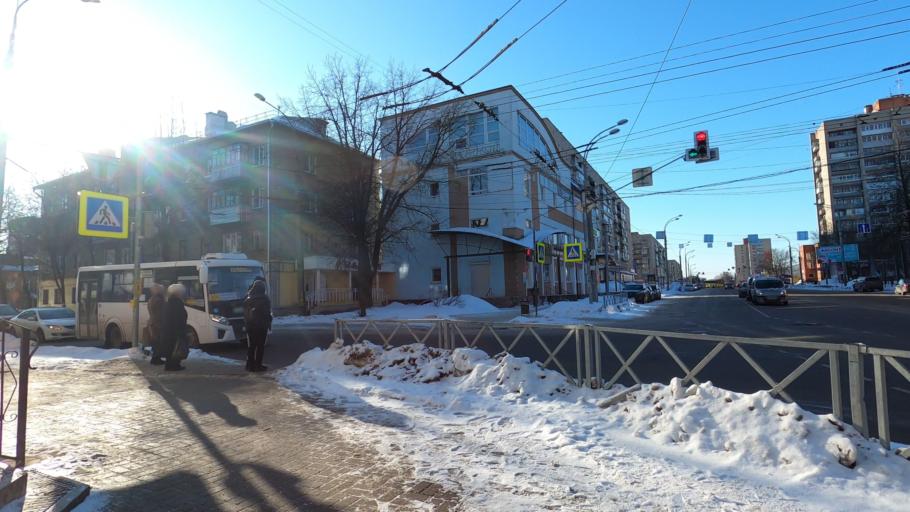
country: RU
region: Jaroslavl
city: Rybinsk
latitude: 58.0482
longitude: 38.8401
